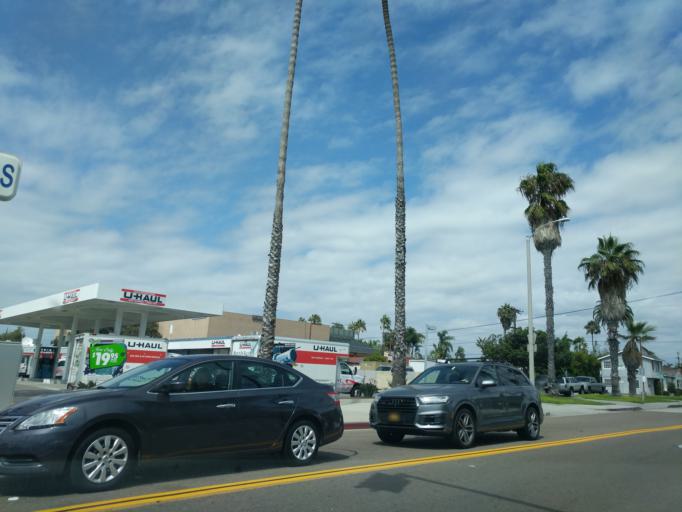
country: US
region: California
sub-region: San Diego County
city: Carlsbad
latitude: 33.1753
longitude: -117.3621
